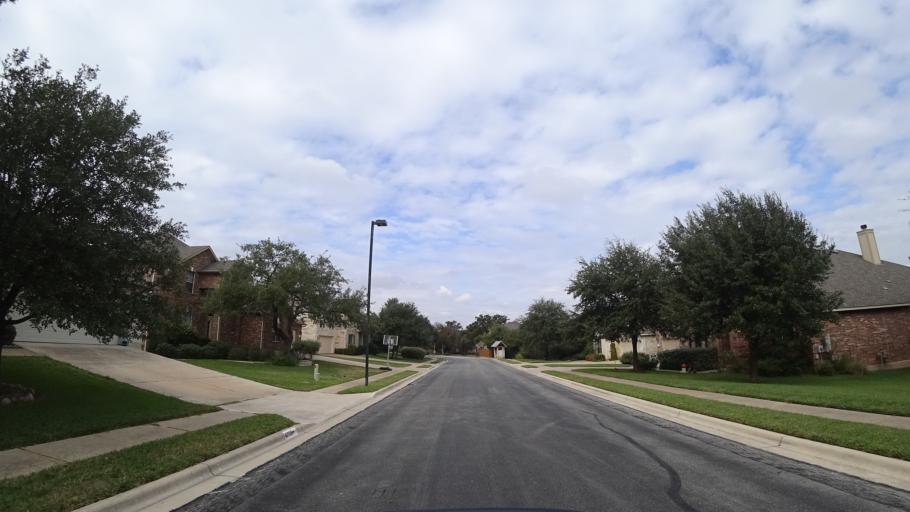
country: US
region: Texas
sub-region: Travis County
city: Shady Hollow
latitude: 30.1900
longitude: -97.9003
